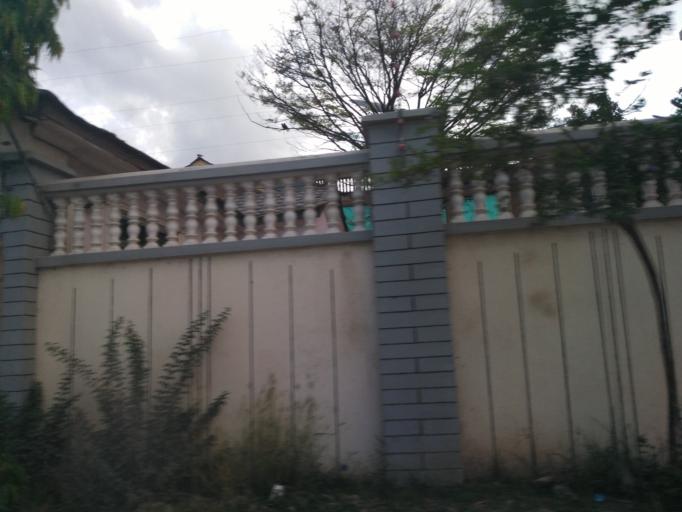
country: TZ
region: Dar es Salaam
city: Magomeni
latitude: -6.7629
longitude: 39.2680
